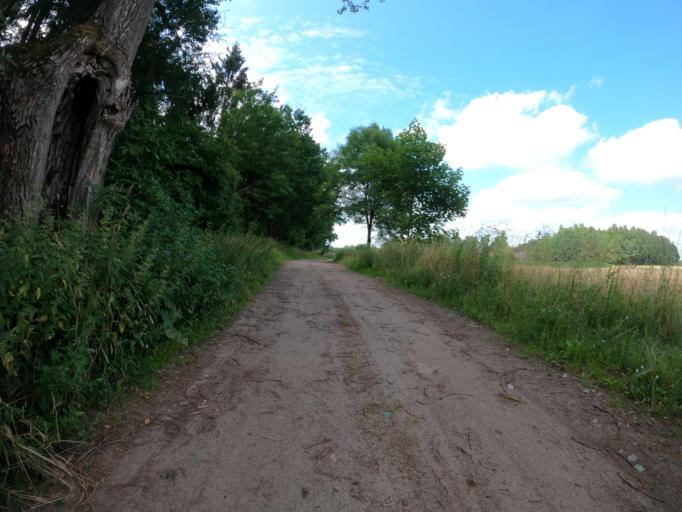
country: PL
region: West Pomeranian Voivodeship
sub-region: Powiat szczecinecki
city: Grzmiaca
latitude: 53.8228
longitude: 16.4801
